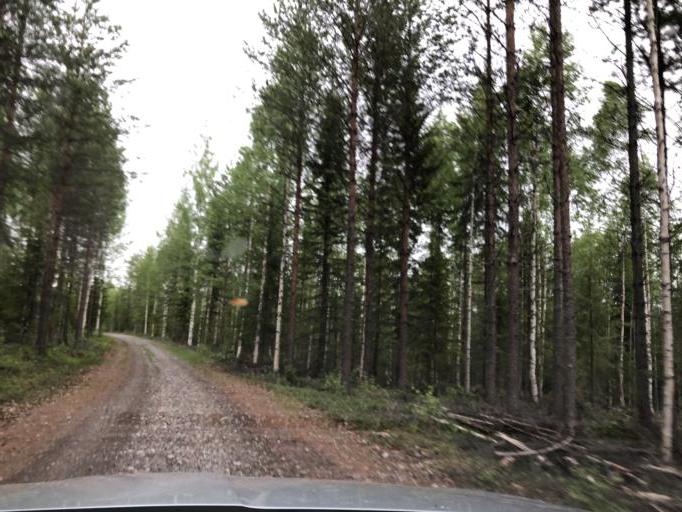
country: SE
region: Norrbotten
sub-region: Pitea Kommun
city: Roknas
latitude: 65.4009
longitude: 21.2626
